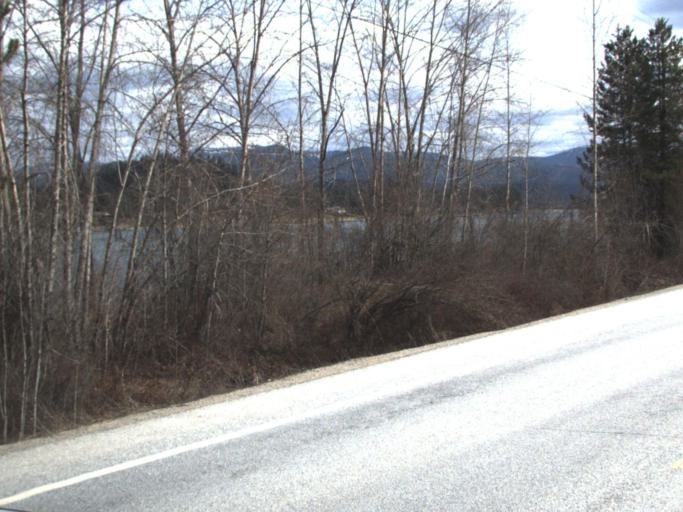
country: US
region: Washington
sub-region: Pend Oreille County
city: Newport
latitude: 48.2316
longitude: -117.2075
